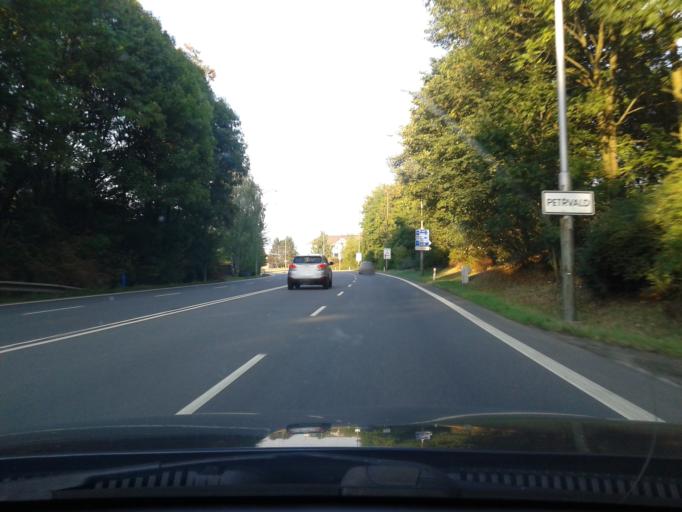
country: CZ
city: Senov
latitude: 49.8186
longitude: 18.3617
